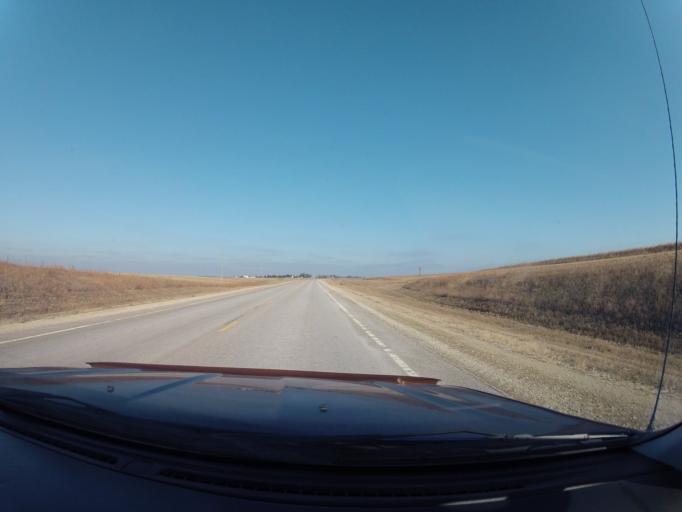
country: US
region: Kansas
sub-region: Marshall County
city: Blue Rapids
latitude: 39.5855
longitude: -96.7503
